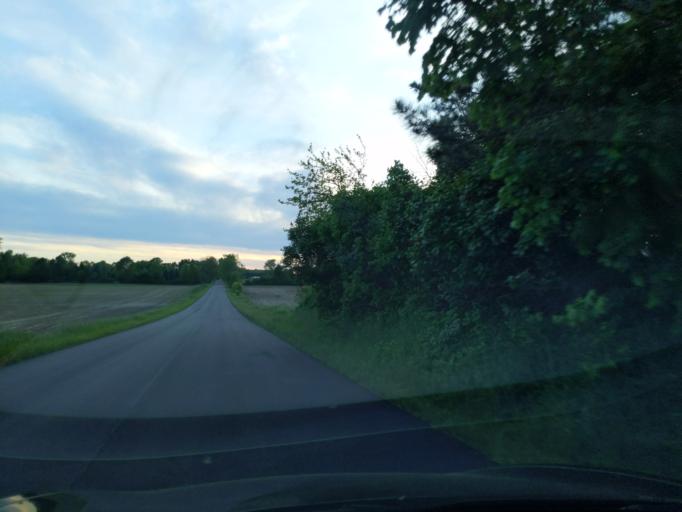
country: US
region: Michigan
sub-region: Ingham County
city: Okemos
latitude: 42.6511
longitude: -84.4236
